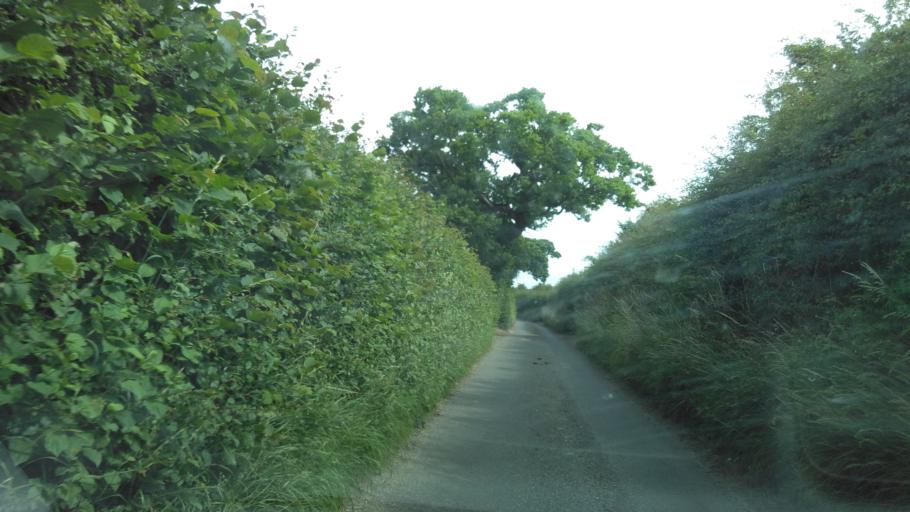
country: GB
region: England
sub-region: Kent
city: Canterbury
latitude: 51.2517
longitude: 1.0564
